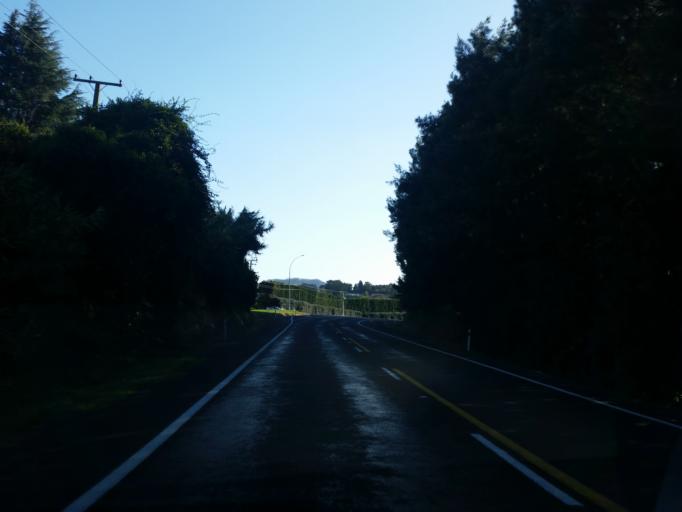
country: NZ
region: Bay of Plenty
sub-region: Western Bay of Plenty District
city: Katikati
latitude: -37.5385
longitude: 175.9120
